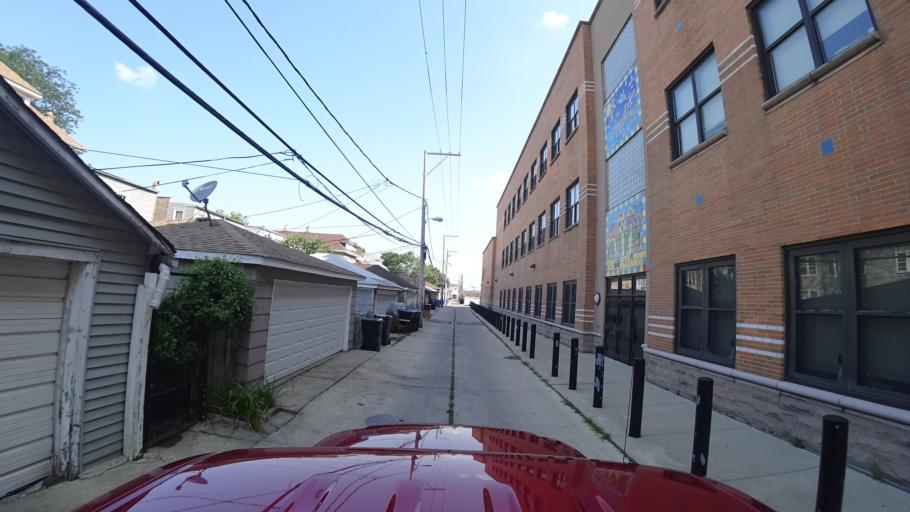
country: US
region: Illinois
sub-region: Cook County
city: Cicero
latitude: 41.8112
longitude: -87.7047
